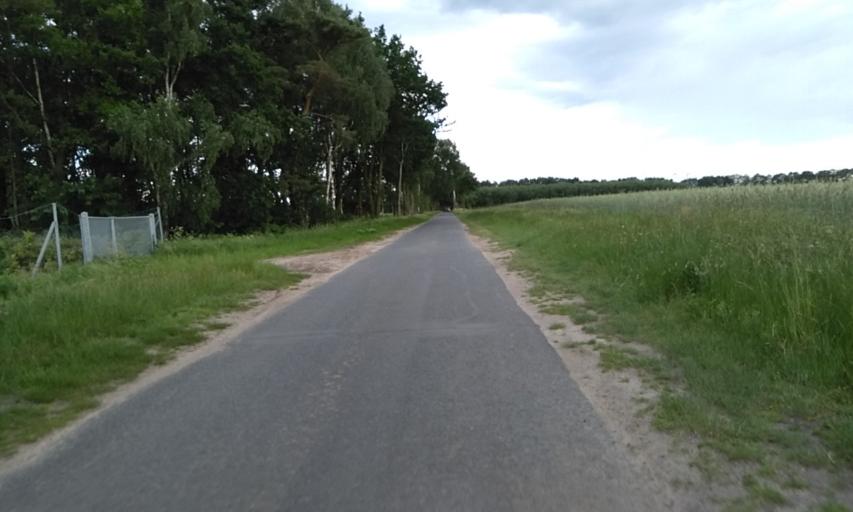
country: DE
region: Lower Saxony
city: Regesbostel
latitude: 53.3874
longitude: 9.6438
